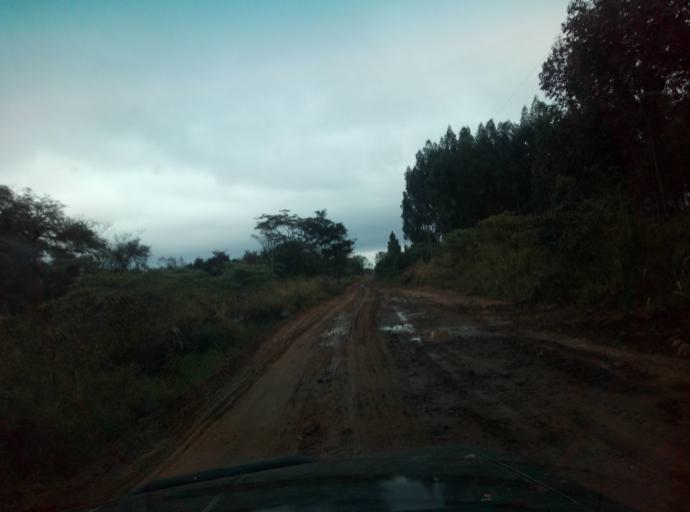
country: PY
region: Caaguazu
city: Carayao
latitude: -25.1902
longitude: -56.3871
